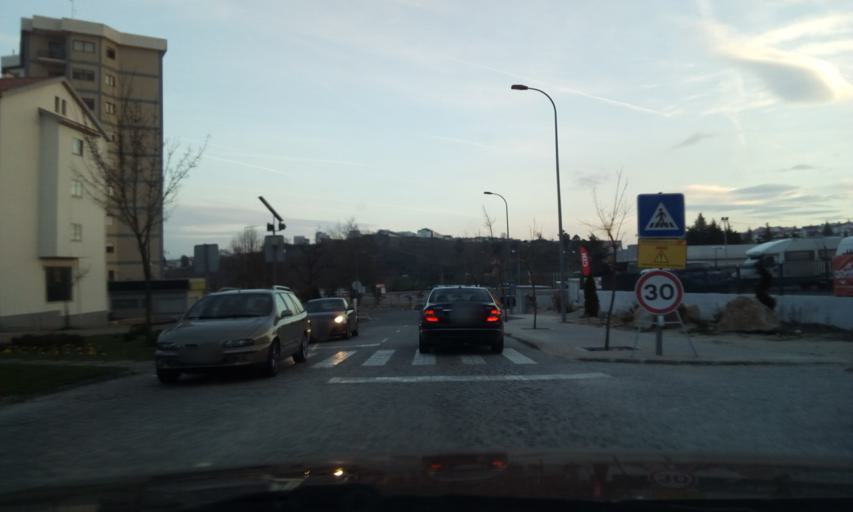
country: PT
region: Guarda
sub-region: Guarda
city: Sequeira
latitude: 40.5516
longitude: -7.2463
